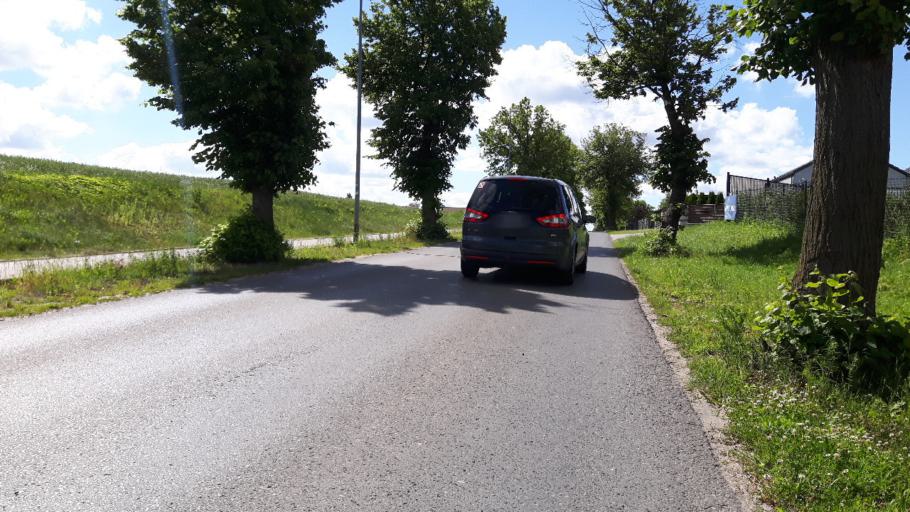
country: PL
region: Pomeranian Voivodeship
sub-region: Powiat pucki
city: Mosty
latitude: 54.6020
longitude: 18.4980
